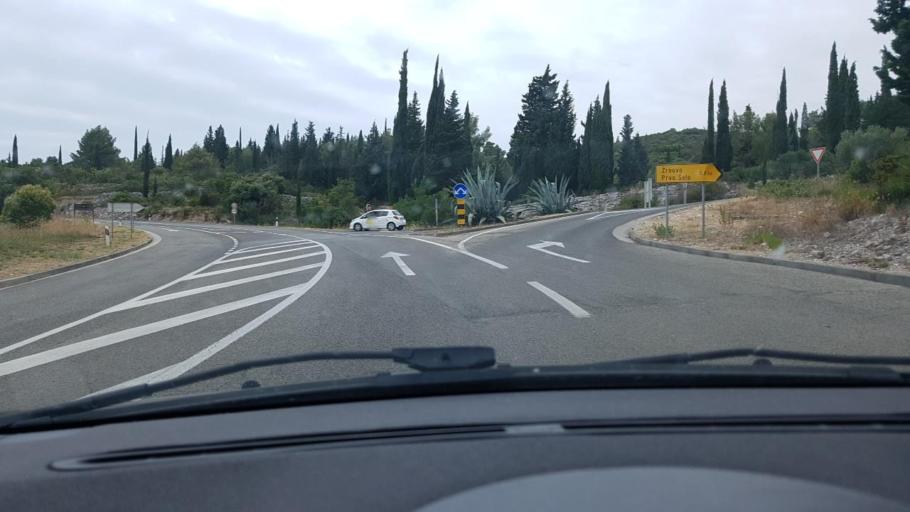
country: HR
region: Dubrovacko-Neretvanska
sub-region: Grad Korcula
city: Zrnovo
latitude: 42.9493
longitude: 17.1203
